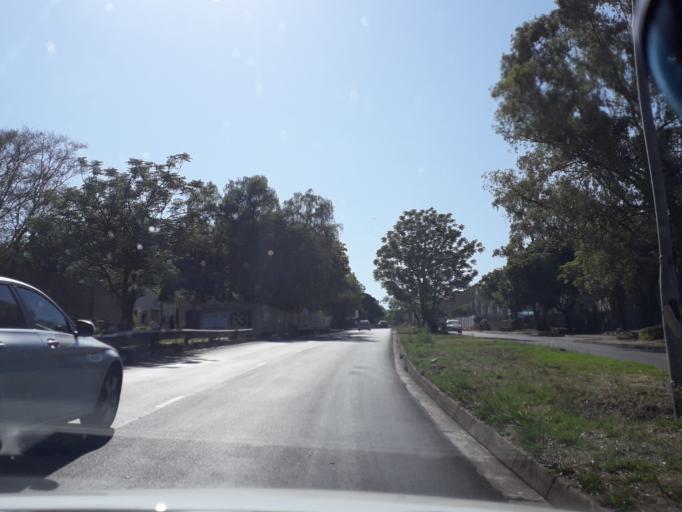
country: ZA
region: Gauteng
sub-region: City of Johannesburg Metropolitan Municipality
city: Johannesburg
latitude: -26.0912
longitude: 27.9910
